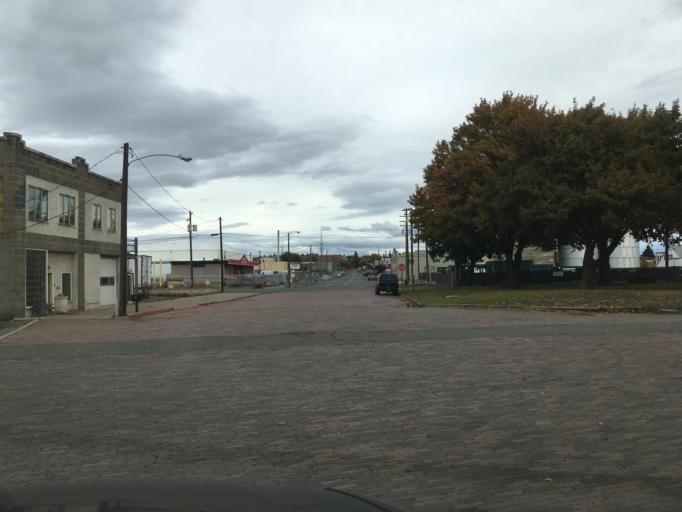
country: US
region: Washington
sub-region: Kittitas County
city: Ellensburg
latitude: 46.9943
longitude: -120.5551
